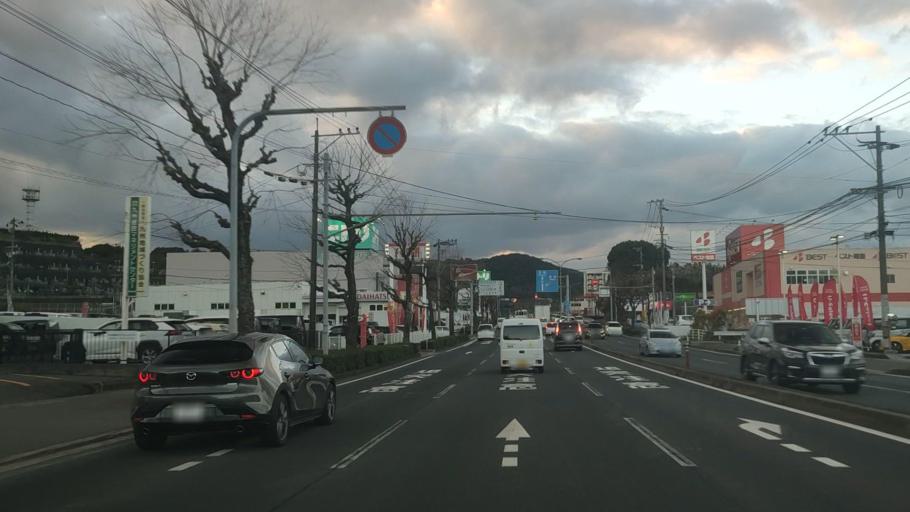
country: JP
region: Nagasaki
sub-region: Isahaya-shi
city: Isahaya
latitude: 32.8296
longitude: 129.9929
